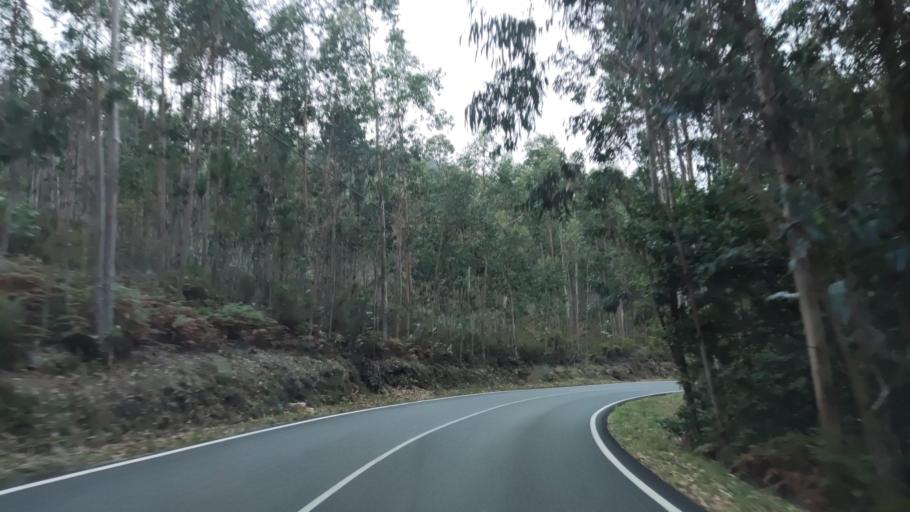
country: ES
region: Galicia
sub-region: Provincia de Pontevedra
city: Catoira
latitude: 42.6599
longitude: -8.7508
